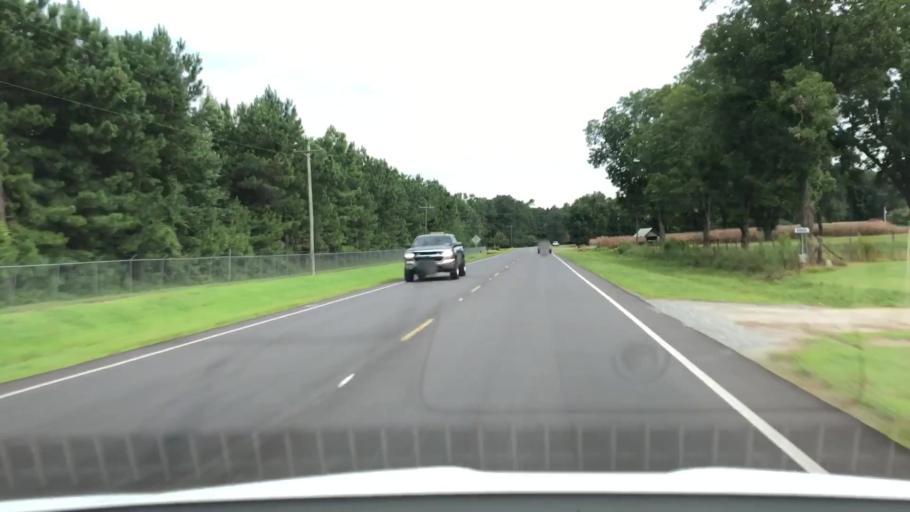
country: US
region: North Carolina
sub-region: Jones County
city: Maysville
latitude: 34.8847
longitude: -77.2108
